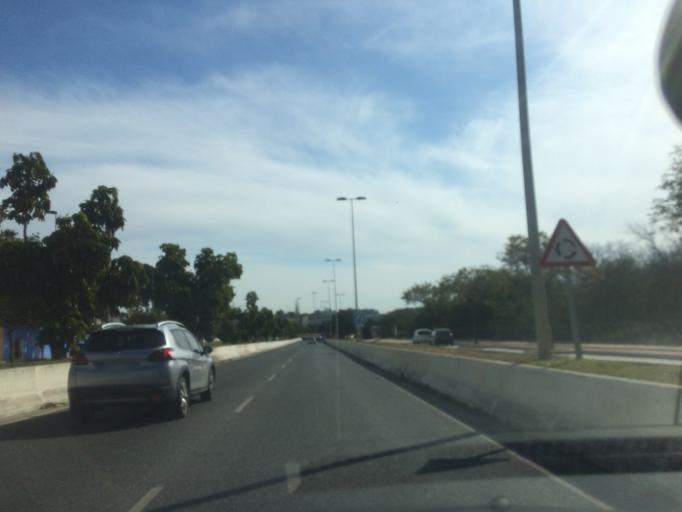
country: ES
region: Andalusia
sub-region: Provincia de Malaga
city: Torremolinos
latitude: 36.6586
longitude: -4.4906
